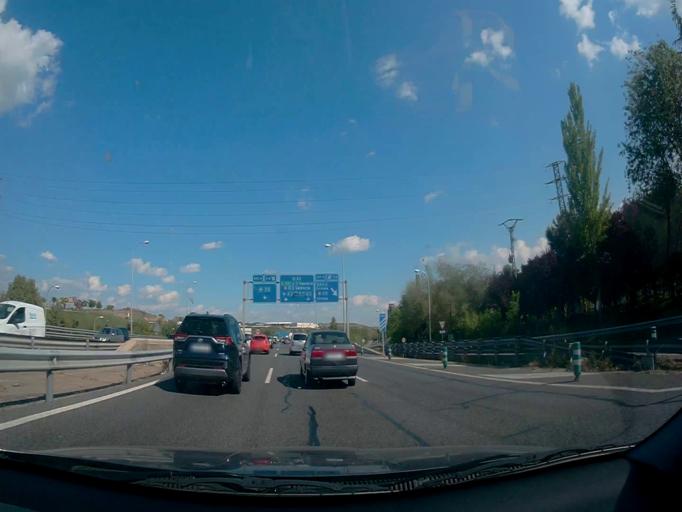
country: ES
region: Madrid
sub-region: Provincia de Madrid
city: Villaverde
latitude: 40.3627
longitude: -3.6859
